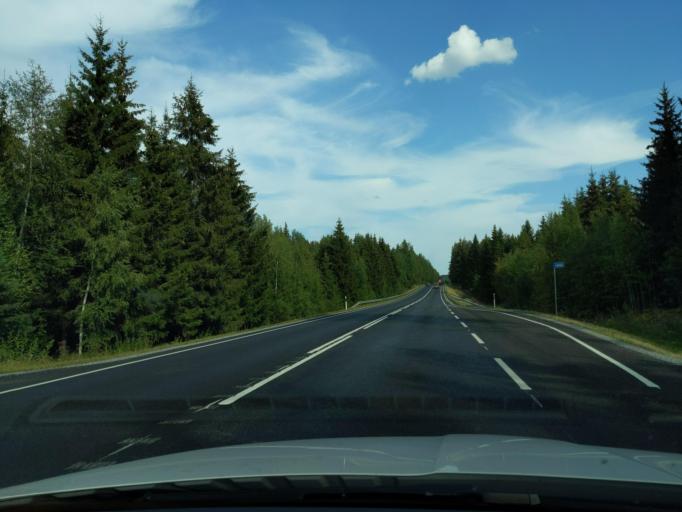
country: FI
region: Haeme
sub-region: Haemeenlinna
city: Tuulos
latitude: 61.1591
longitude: 24.6882
